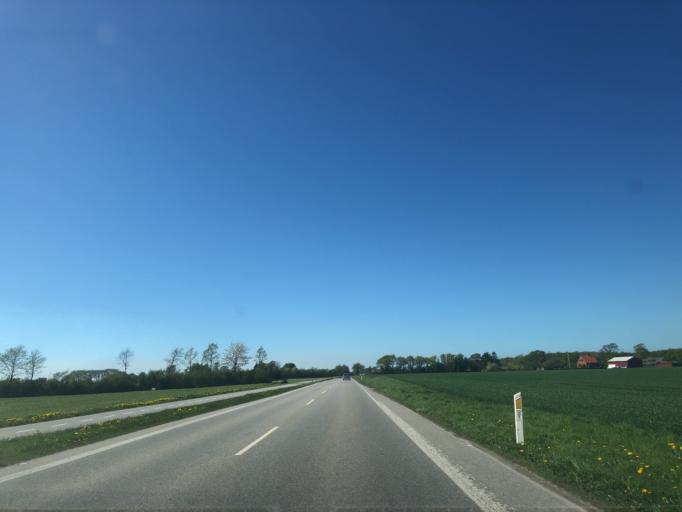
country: DK
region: Zealand
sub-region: Stevns Kommune
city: Store Heddinge
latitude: 55.3326
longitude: 12.3573
